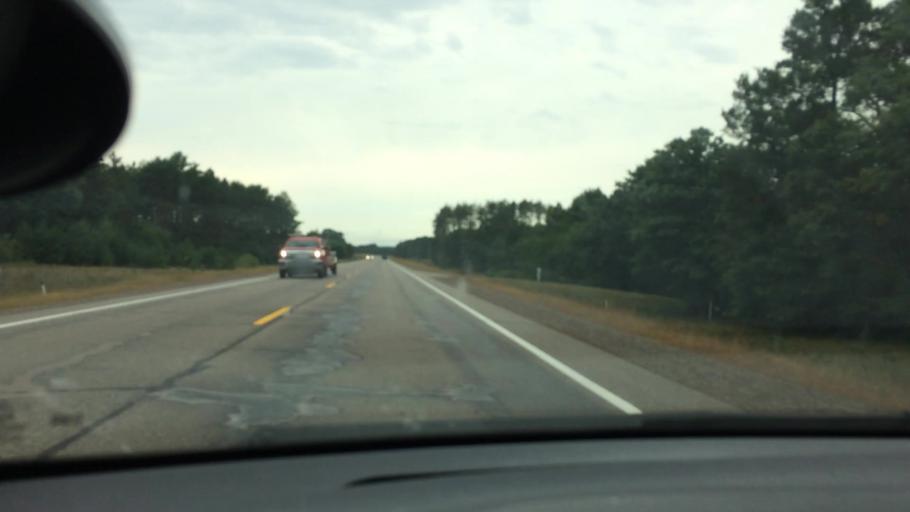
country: US
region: Wisconsin
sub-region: Eau Claire County
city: Augusta
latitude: 44.5824
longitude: -91.0868
